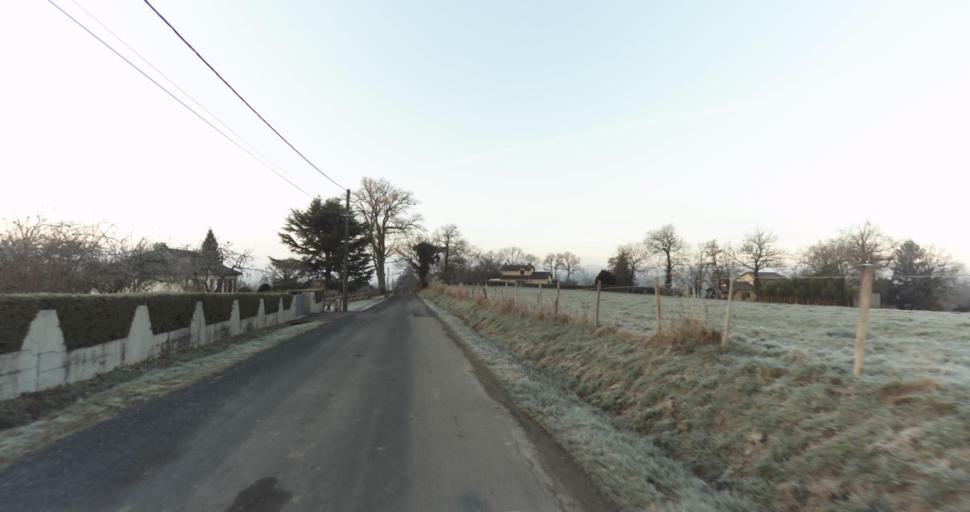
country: FR
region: Limousin
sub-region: Departement de la Haute-Vienne
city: Aixe-sur-Vienne
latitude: 45.8054
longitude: 1.1284
